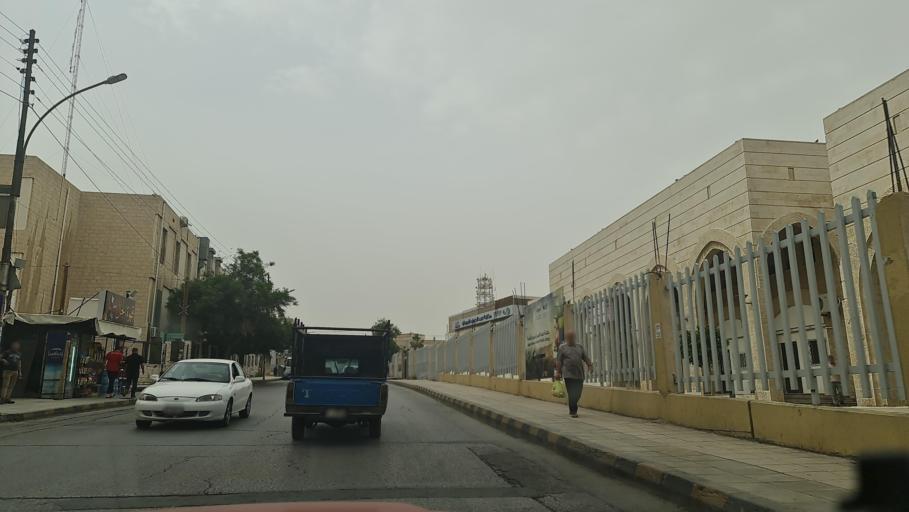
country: JO
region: Amman
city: Amman
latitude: 31.9393
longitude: 35.9384
